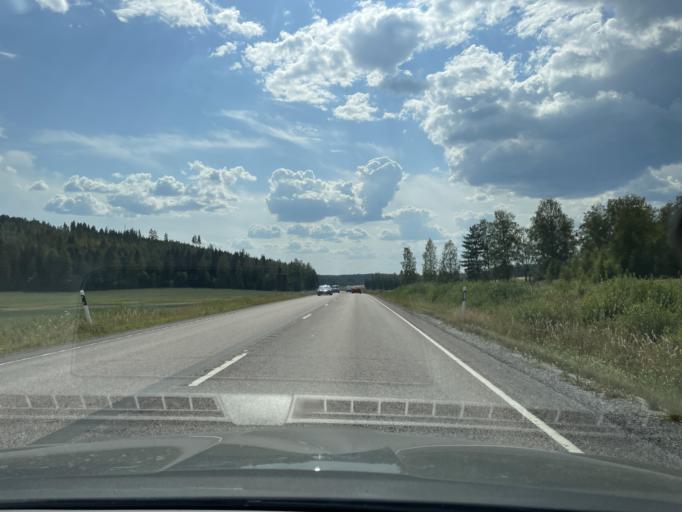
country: FI
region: Central Finland
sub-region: Jyvaeskylae
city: Korpilahti
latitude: 61.9667
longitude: 25.3805
